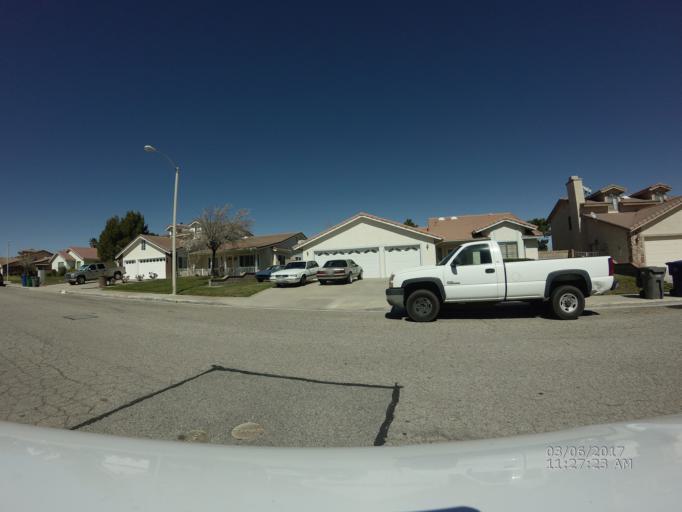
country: US
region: California
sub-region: Los Angeles County
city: Quartz Hill
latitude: 34.6502
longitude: -118.2418
